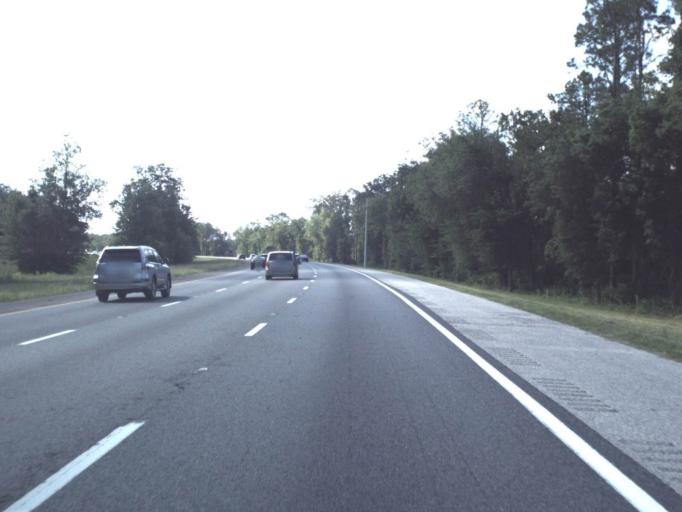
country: US
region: Florida
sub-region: Saint Johns County
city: Butler Beach
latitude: 29.6820
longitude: -81.3197
